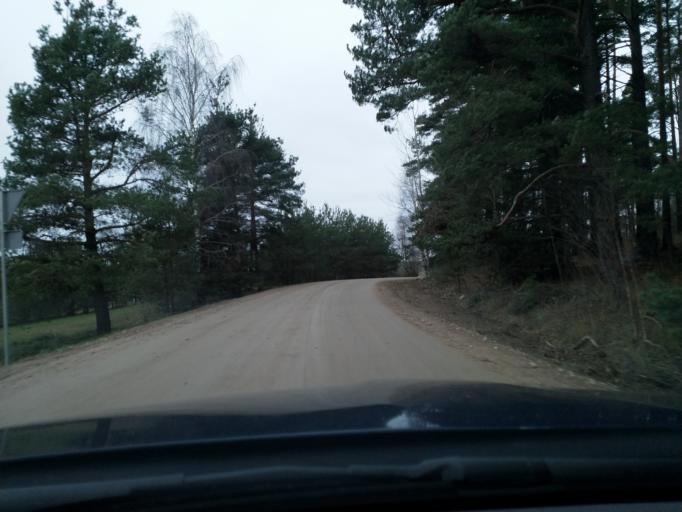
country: LV
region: Ventspils Rajons
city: Piltene
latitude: 57.1274
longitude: 21.8040
